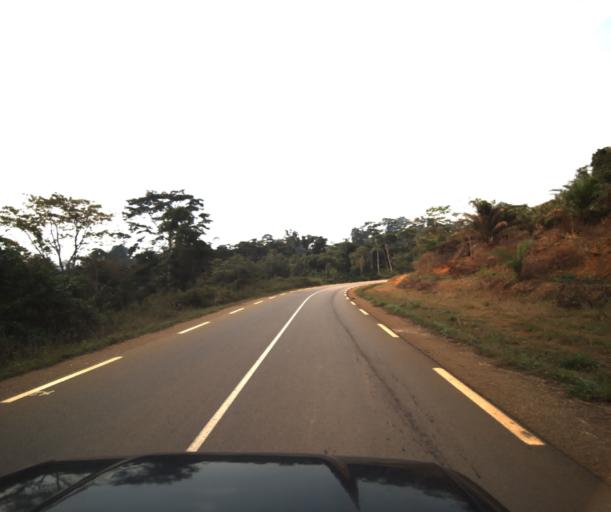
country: CM
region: Centre
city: Mbankomo
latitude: 3.6642
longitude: 11.3428
